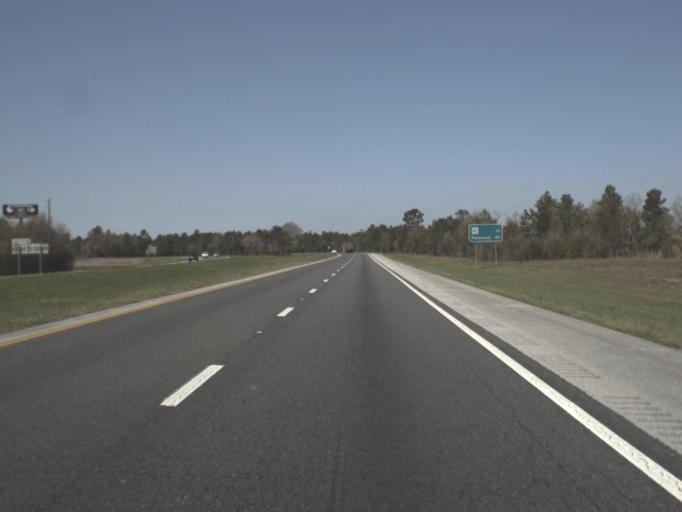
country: US
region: Florida
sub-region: Okaloosa County
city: Crestview
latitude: 30.7336
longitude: -86.3668
